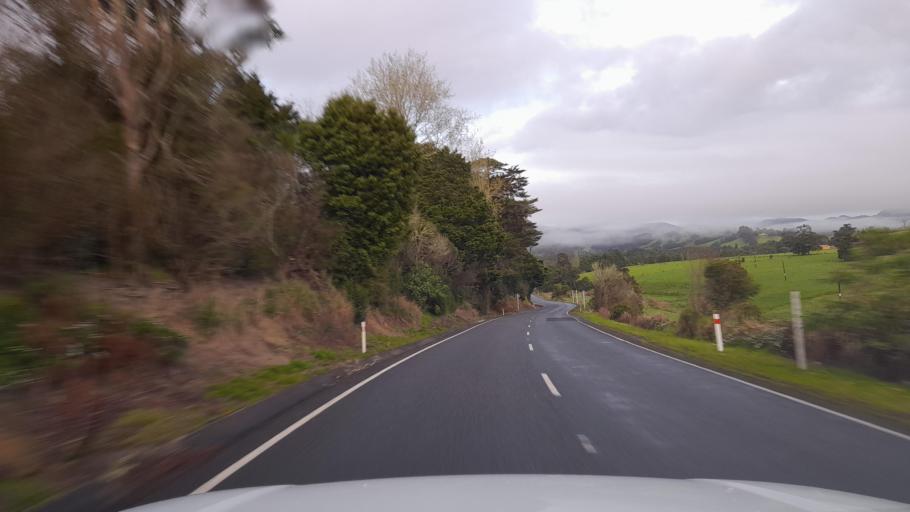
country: NZ
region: Northland
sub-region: Kaipara District
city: Dargaville
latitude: -35.7147
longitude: 173.9528
